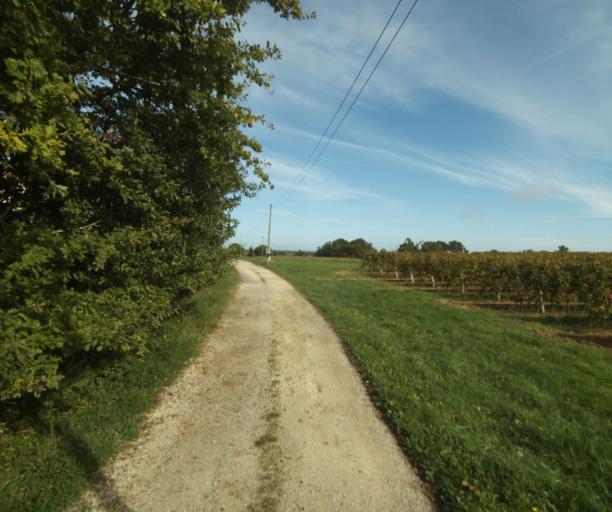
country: FR
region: Midi-Pyrenees
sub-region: Departement du Gers
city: Eauze
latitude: 43.9335
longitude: 0.1136
